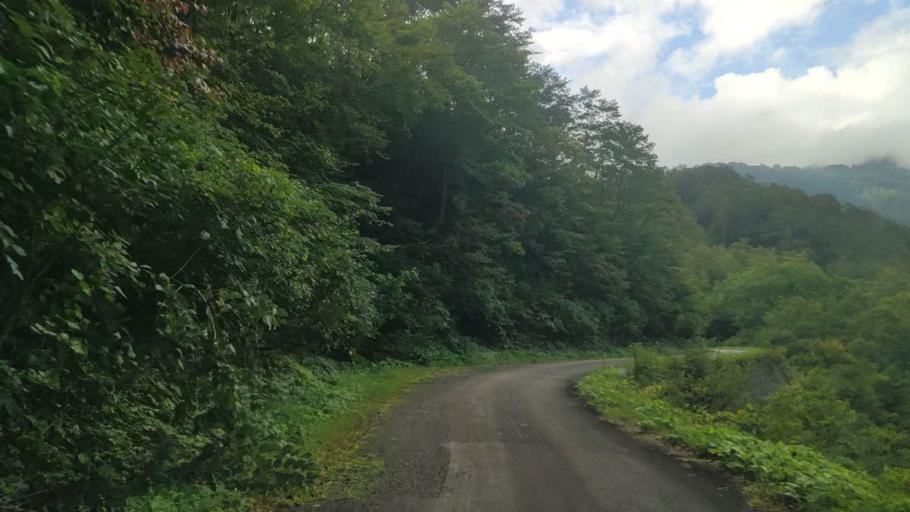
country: JP
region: Toyama
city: Yatsuomachi-higashikumisaka
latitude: 36.3504
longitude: 137.0646
